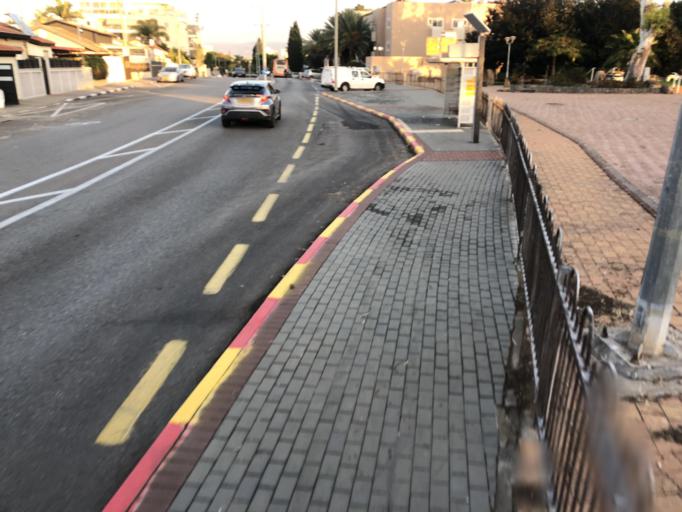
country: IL
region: Northern District
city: `Akko
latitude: 32.9278
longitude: 35.0899
